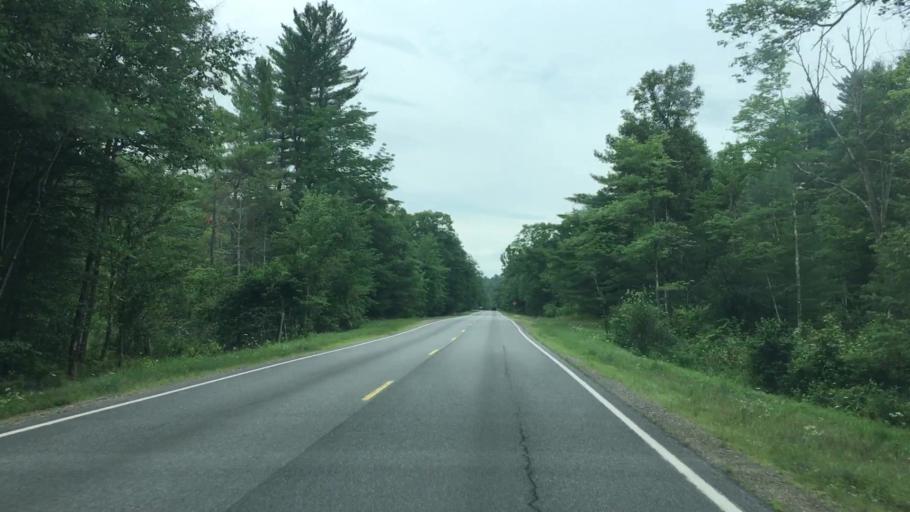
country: US
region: New York
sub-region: Clinton County
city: Peru
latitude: 44.4843
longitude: -73.5958
